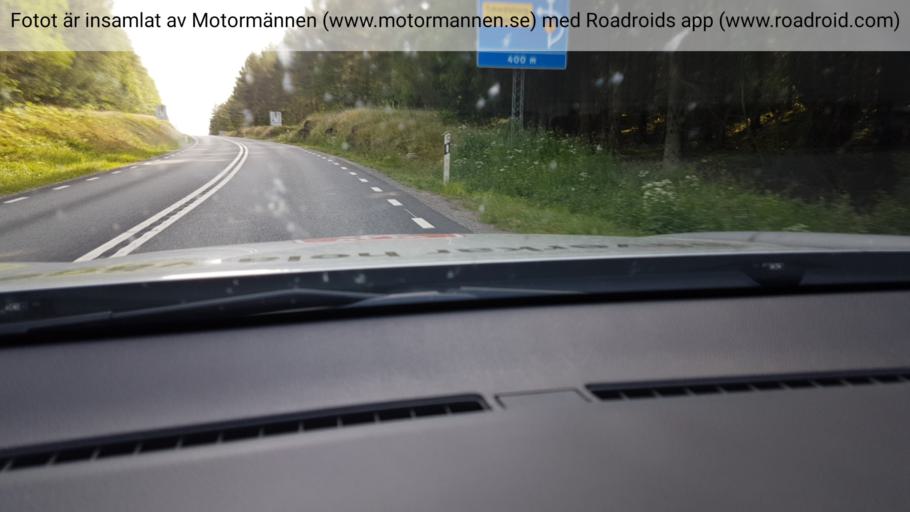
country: SE
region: Joenkoeping
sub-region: Aneby Kommun
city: Aneby
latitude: 57.8722
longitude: 14.8702
